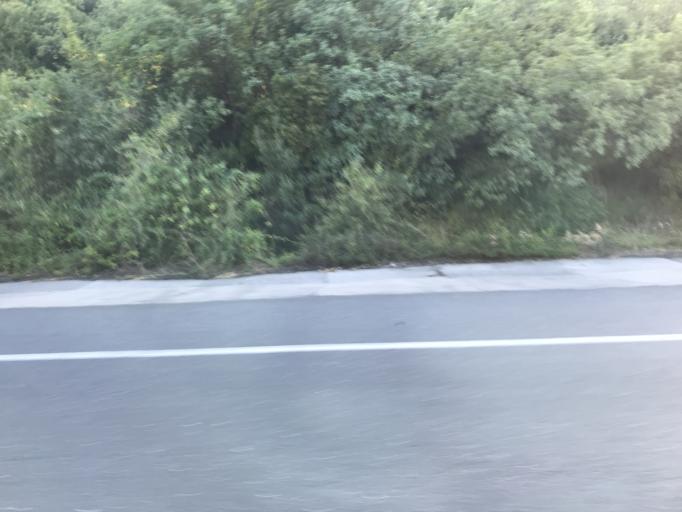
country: TR
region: Kocaeli
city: Gebze
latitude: 40.7741
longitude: 29.4243
